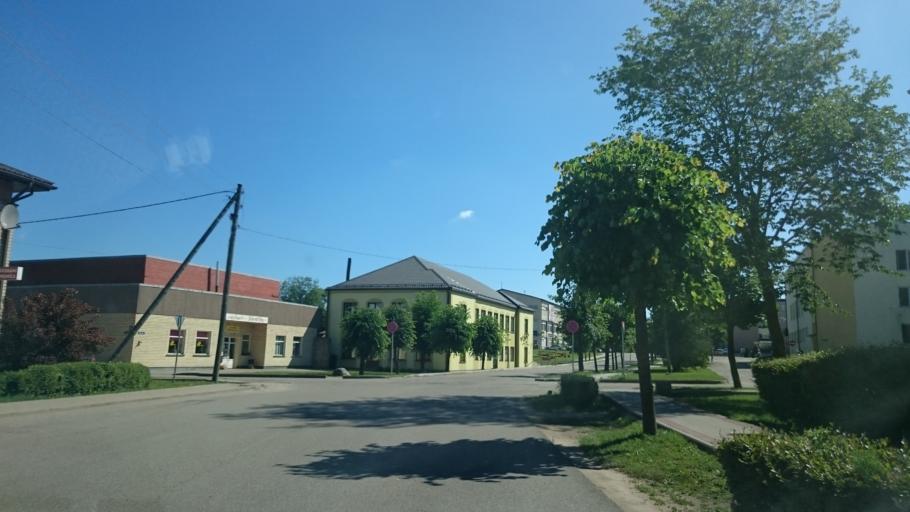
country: LV
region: Ludzas Rajons
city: Ludza
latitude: 56.5438
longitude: 27.7180
